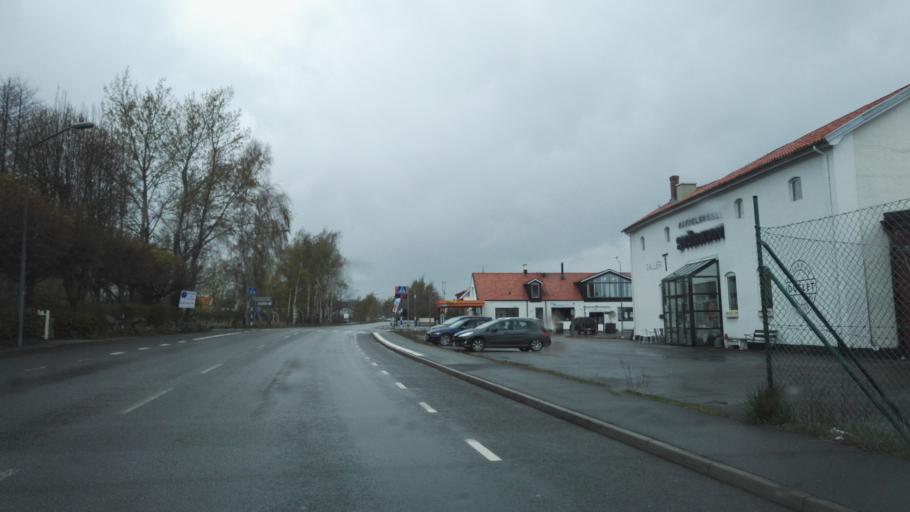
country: SE
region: Skane
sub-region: Simrishamns Kommun
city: Kivik
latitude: 55.6835
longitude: 14.2231
